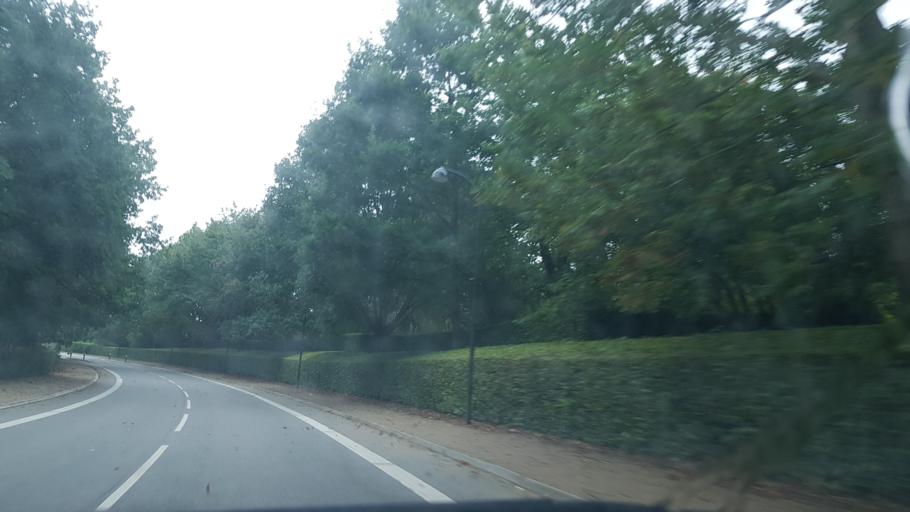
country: DK
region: Capital Region
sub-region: Rudersdal Kommune
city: Trorod
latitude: 55.8365
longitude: 12.5622
